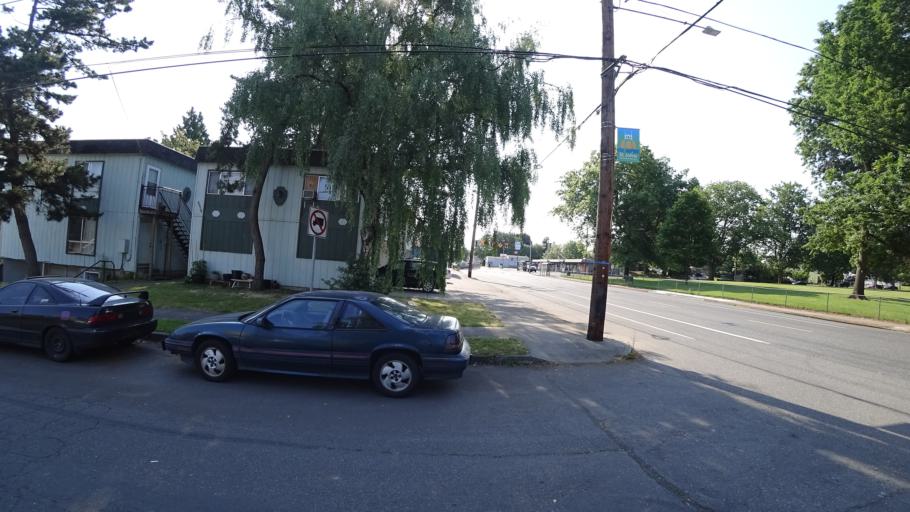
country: US
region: Oregon
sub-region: Washington County
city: West Haven
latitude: 45.5946
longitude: -122.7393
